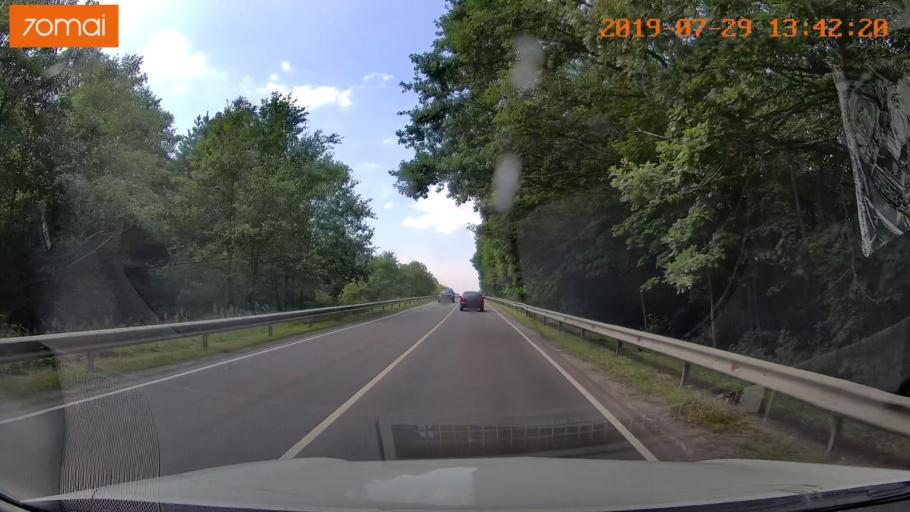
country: RU
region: Kaliningrad
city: Svetlyy
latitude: 54.7367
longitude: 20.1138
